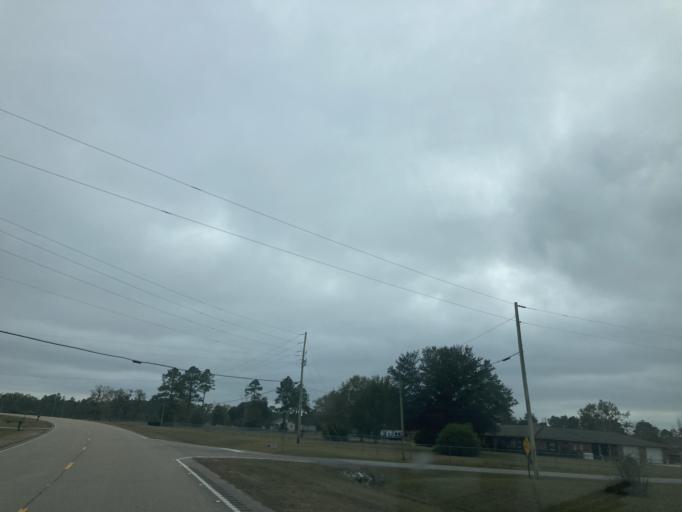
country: US
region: Mississippi
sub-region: Jackson County
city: Latimer
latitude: 30.5428
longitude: -88.9276
